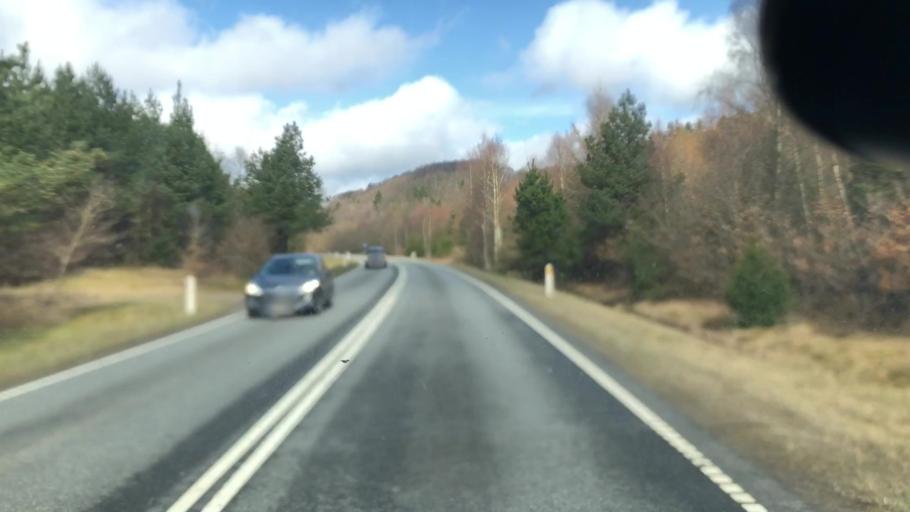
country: DK
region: Central Jutland
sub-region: Silkeborg Kommune
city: Virklund
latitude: 56.0710
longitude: 9.5780
